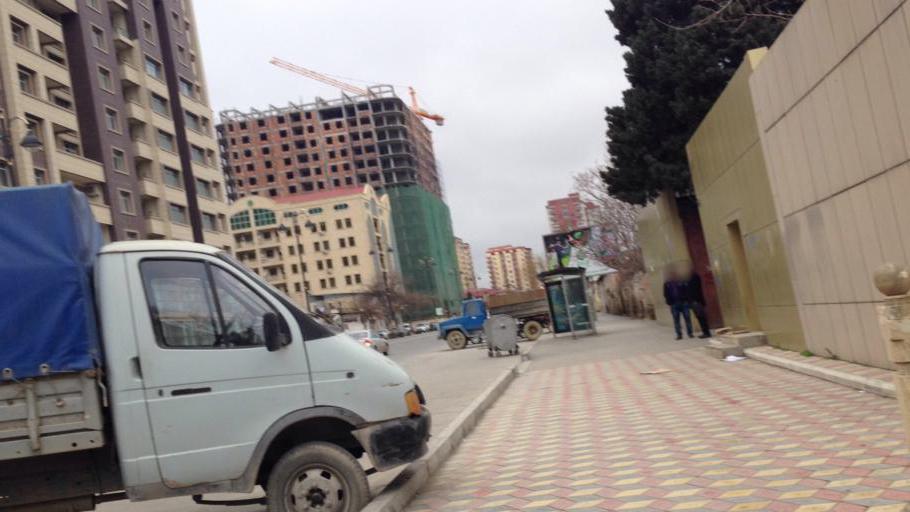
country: AZ
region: Baki
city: Baku
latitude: 40.3972
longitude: 49.8435
